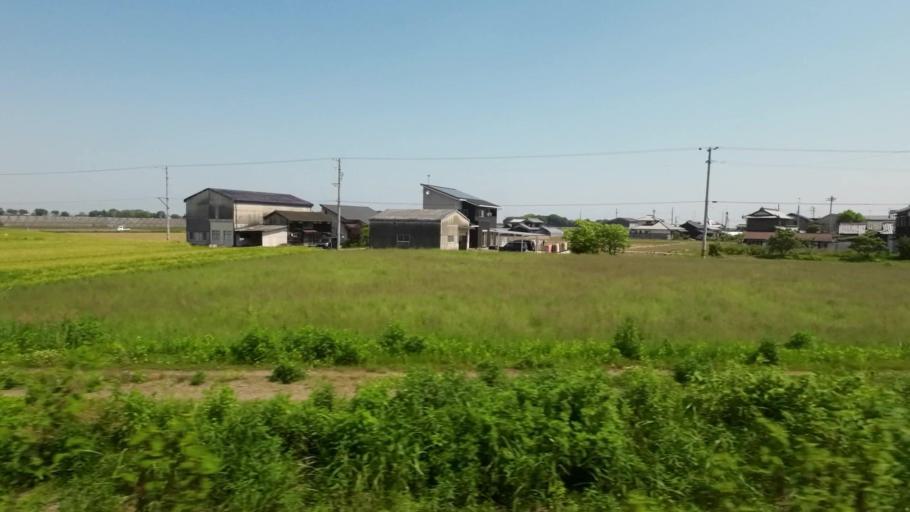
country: JP
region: Ehime
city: Saijo
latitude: 33.8986
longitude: 133.1039
